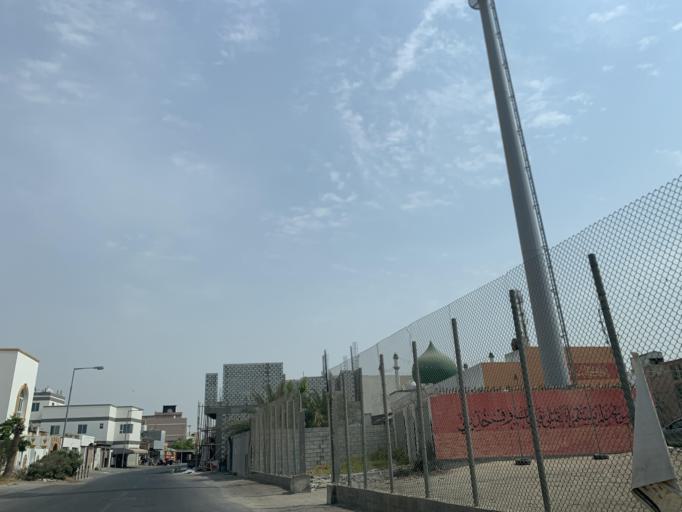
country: BH
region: Manama
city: Jidd Hafs
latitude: 26.2131
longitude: 50.4883
